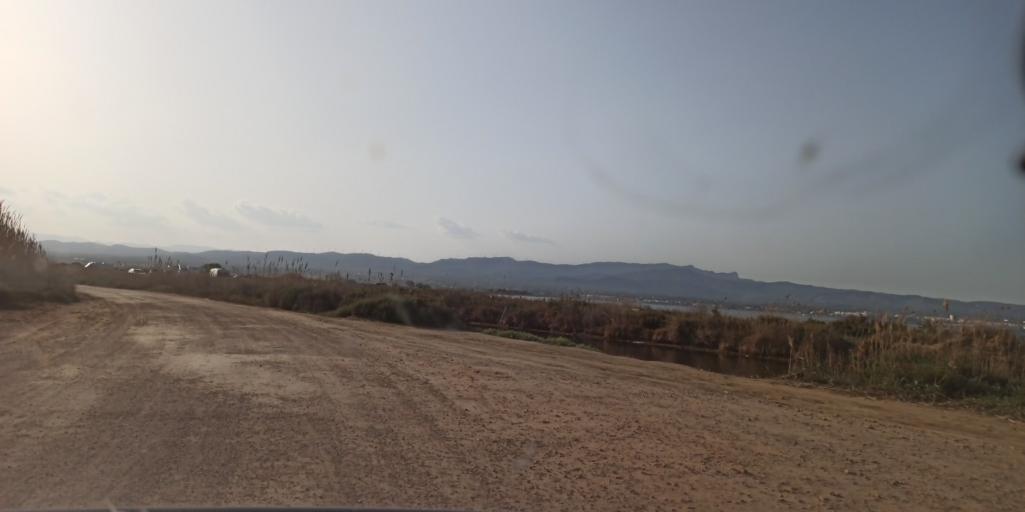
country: ES
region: Catalonia
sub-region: Provincia de Tarragona
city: L'Ampolla
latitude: 40.7784
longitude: 0.7205
